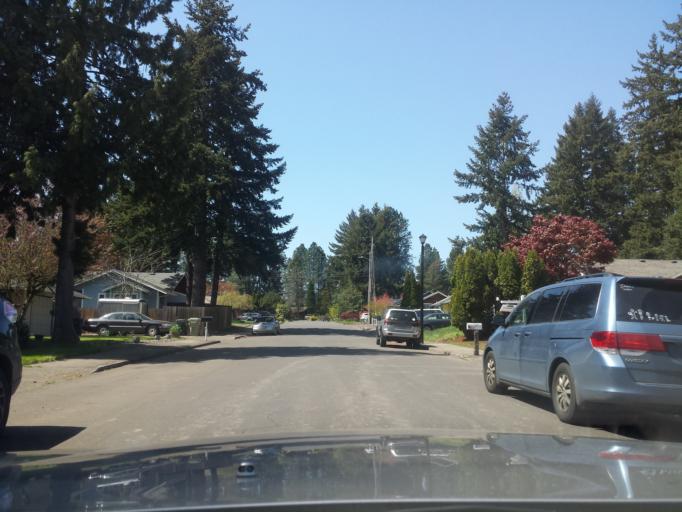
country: US
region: Oregon
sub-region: Washington County
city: Aloha
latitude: 45.4886
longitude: -122.8615
